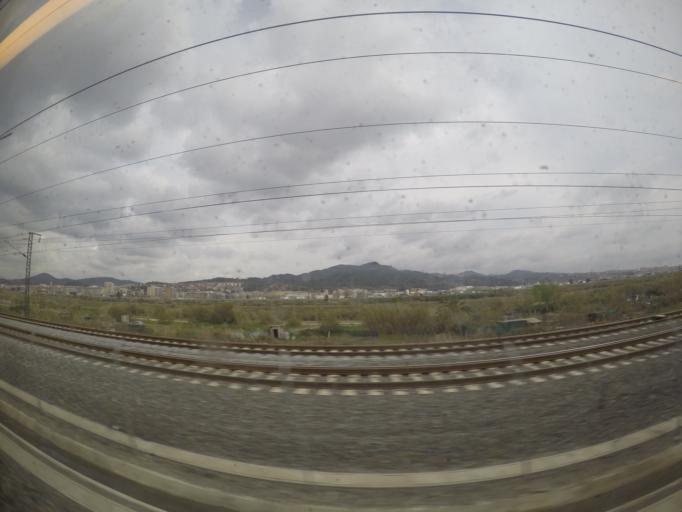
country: ES
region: Catalonia
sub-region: Provincia de Barcelona
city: Sant Vicenc dels Horts
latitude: 41.3995
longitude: 2.0151
